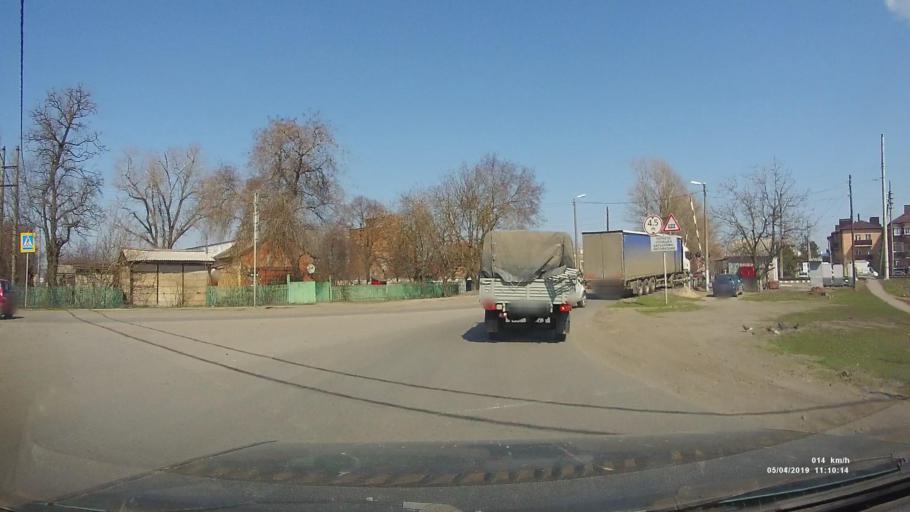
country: RU
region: Rostov
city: Azov
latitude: 47.0921
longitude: 39.4320
